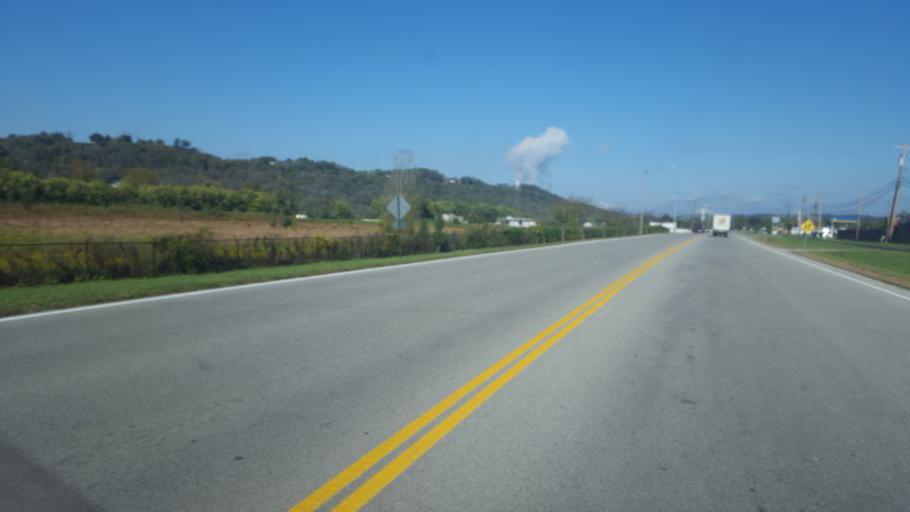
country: US
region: Ohio
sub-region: Brown County
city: Aberdeen
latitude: 38.6626
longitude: -83.7687
